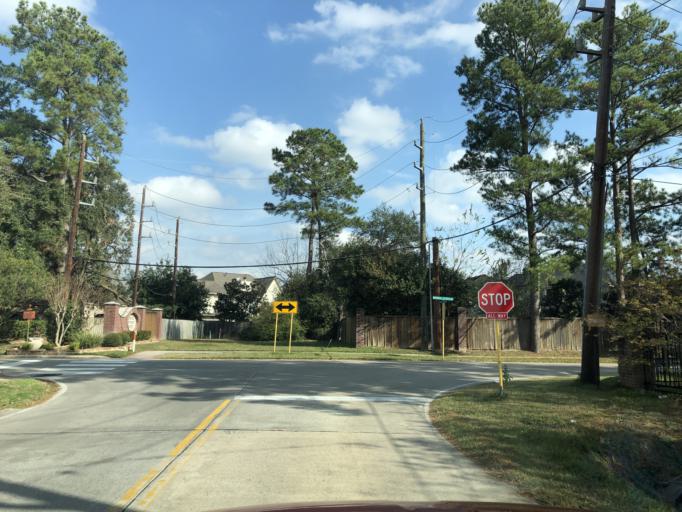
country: US
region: Texas
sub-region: Harris County
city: Tomball
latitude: 30.0293
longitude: -95.5446
